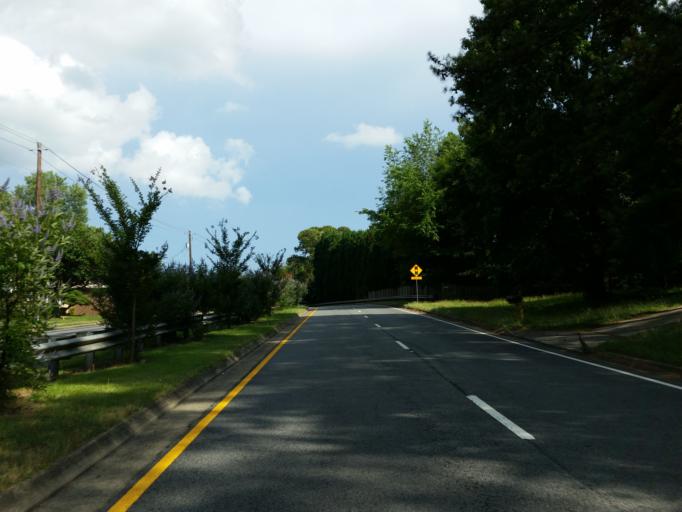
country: US
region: Georgia
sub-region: Cobb County
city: Marietta
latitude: 34.0191
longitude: -84.5118
